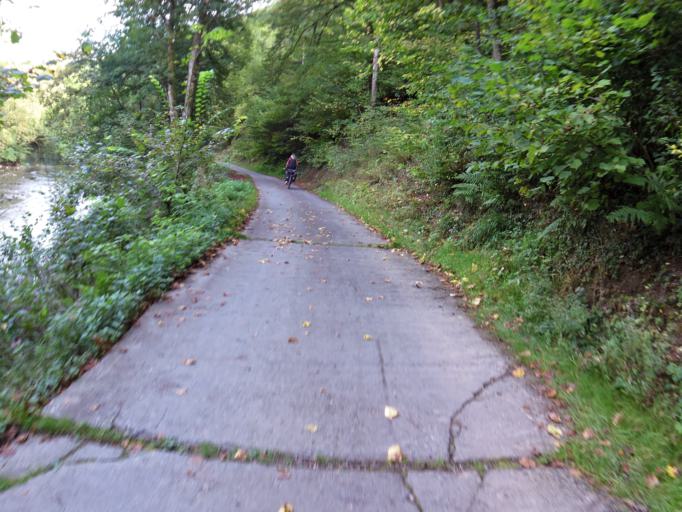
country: DE
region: Baden-Wuerttemberg
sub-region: Freiburg Region
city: Villingendorf
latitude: 48.2042
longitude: 8.6072
